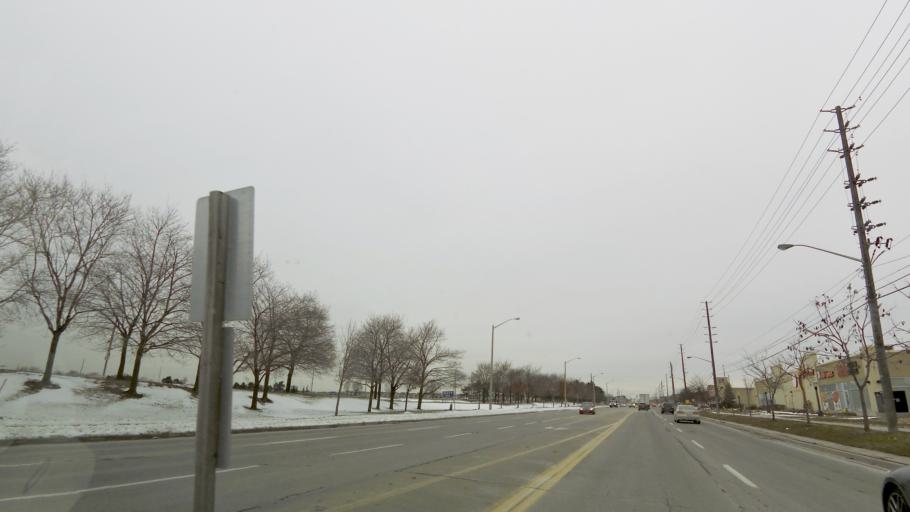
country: CA
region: Ontario
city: Vaughan
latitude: 43.8467
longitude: -79.5360
